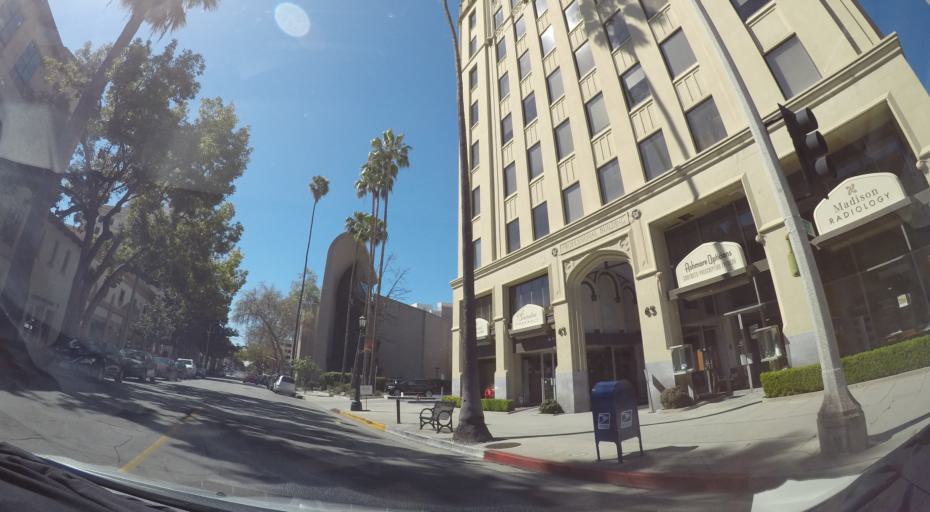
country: US
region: California
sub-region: Los Angeles County
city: Pasadena
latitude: 34.1471
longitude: -118.1384
